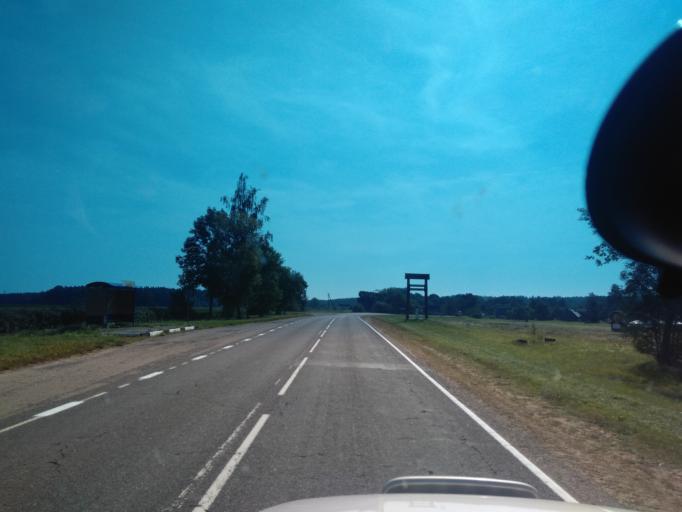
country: BY
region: Minsk
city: Uzda
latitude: 53.3913
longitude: 27.2402
